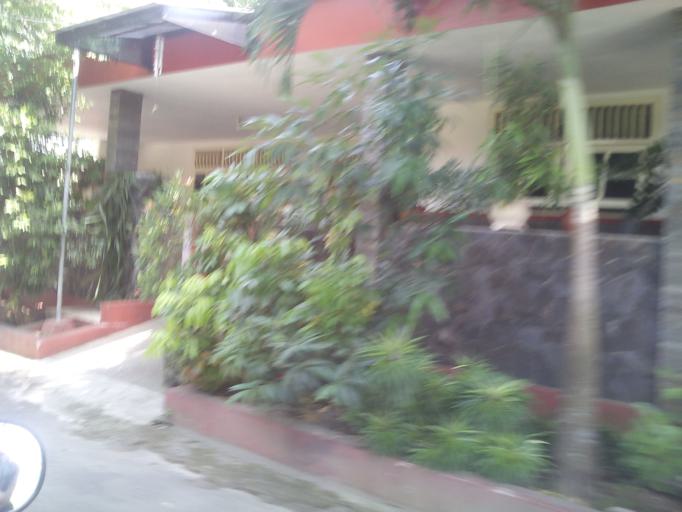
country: ID
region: East Java
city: Sumbersari Wetan
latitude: -8.1770
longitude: 113.7199
